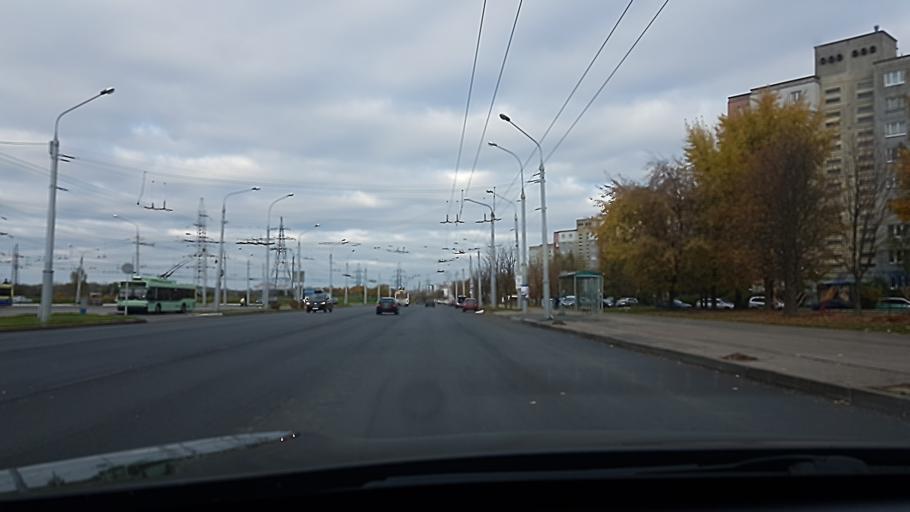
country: BY
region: Minsk
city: Novoye Medvezhino
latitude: 53.8701
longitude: 27.4605
